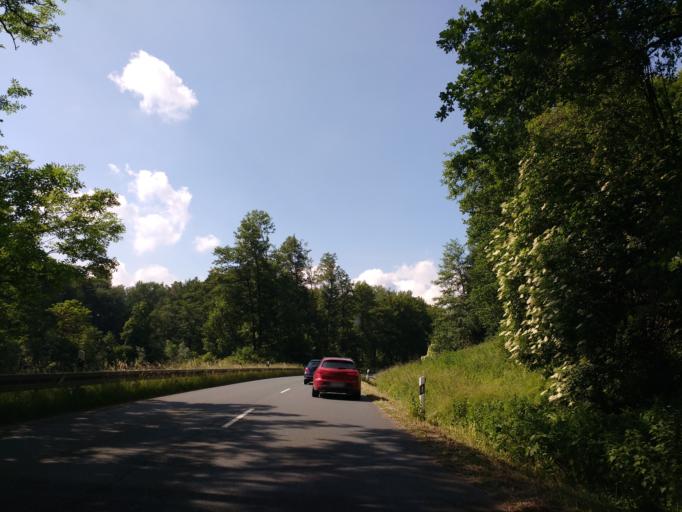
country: DE
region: North Rhine-Westphalia
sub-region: Regierungsbezirk Detmold
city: Dorentrup
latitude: 52.1178
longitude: 8.9492
